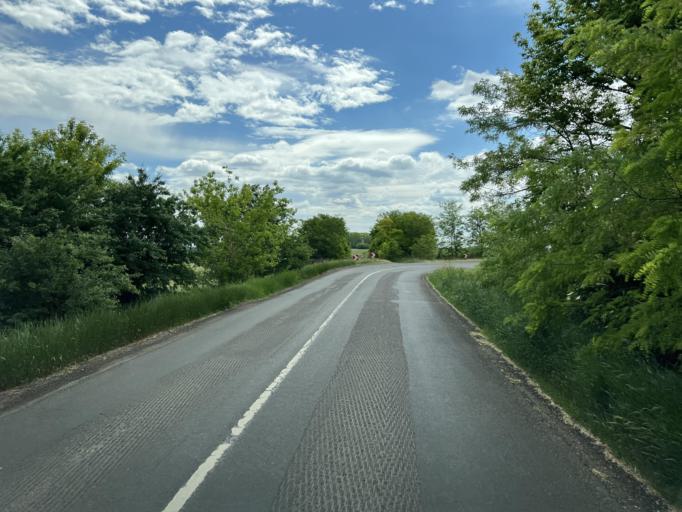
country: HU
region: Pest
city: Szentlorinckata
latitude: 47.4933
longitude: 19.7379
